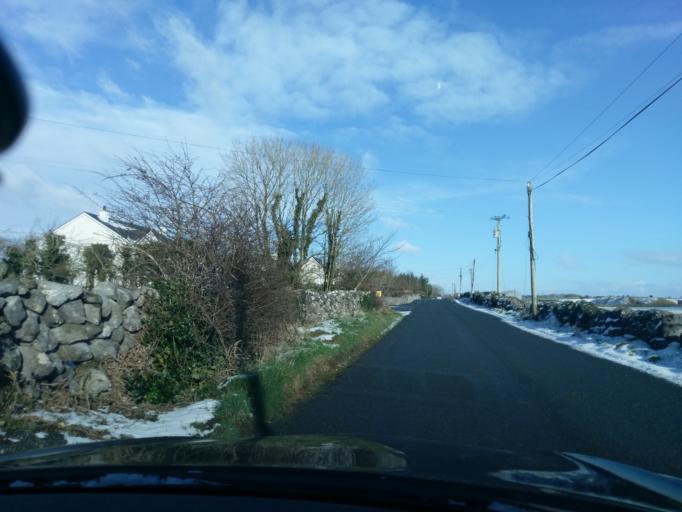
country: IE
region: Connaught
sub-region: County Galway
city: Oranmore
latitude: 53.1981
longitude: -8.8246
